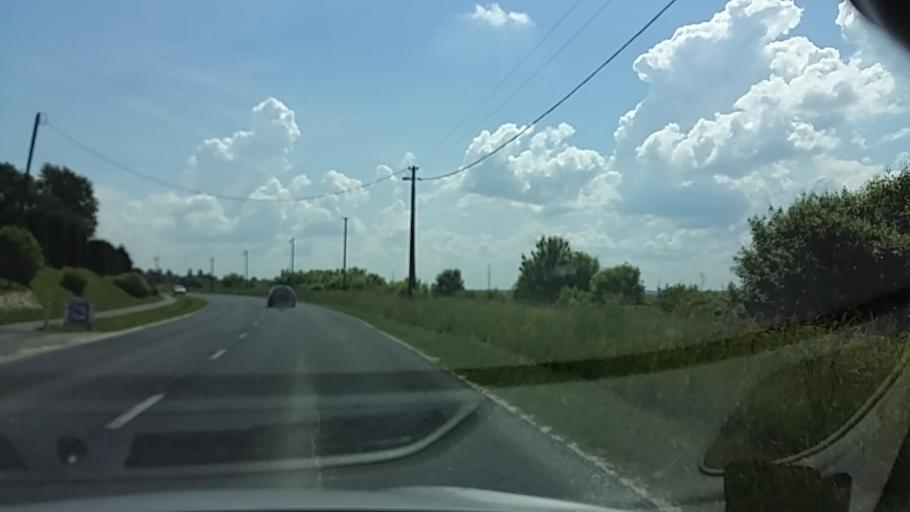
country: AT
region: Burgenland
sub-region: Politischer Bezirk Gussing
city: Inzenhof
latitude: 46.9772
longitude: 16.3550
